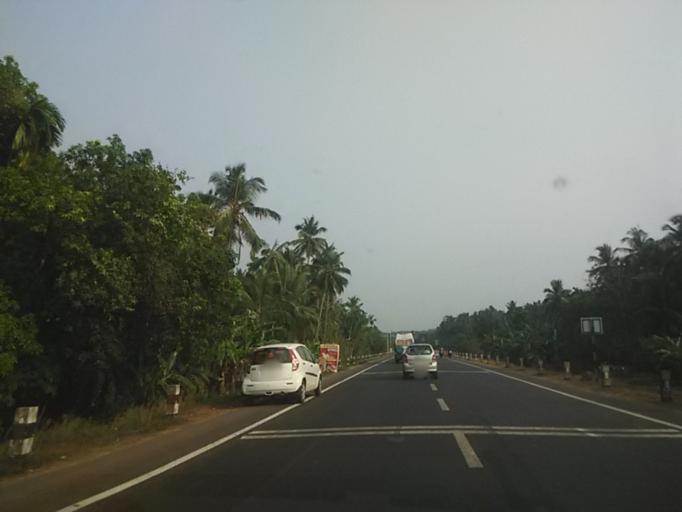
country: IN
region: Kerala
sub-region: Kozhikode
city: Kozhikode
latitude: 11.3153
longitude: 75.7798
